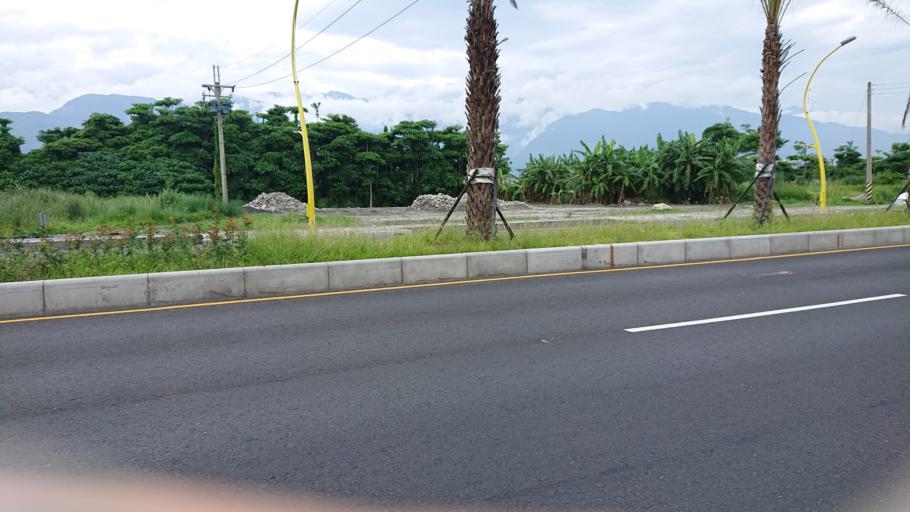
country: TW
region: Taiwan
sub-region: Hualien
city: Hualian
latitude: 23.9540
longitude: 121.6009
